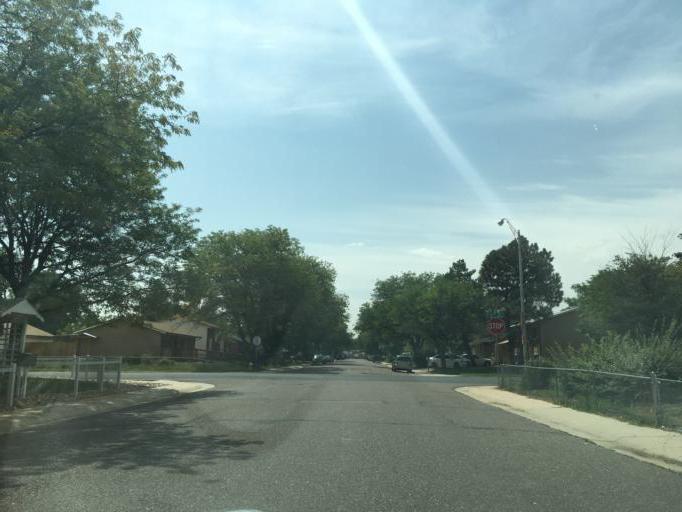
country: US
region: Colorado
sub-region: Adams County
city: Aurora
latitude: 39.7333
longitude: -104.7931
